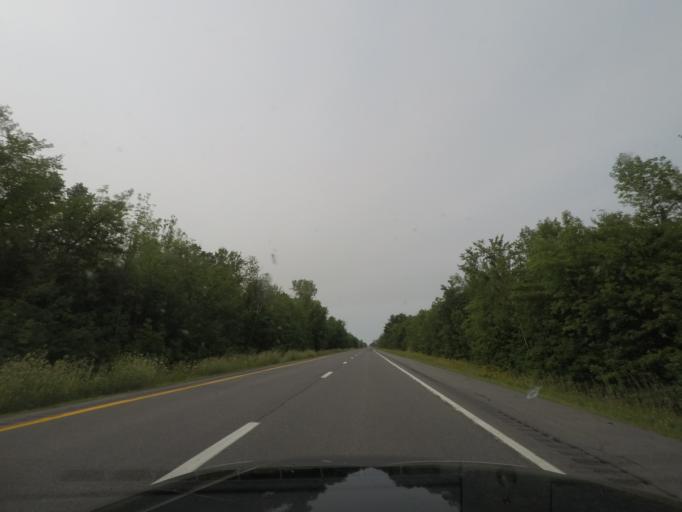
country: US
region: New York
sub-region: Clinton County
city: Champlain
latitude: 44.9336
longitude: -73.4465
